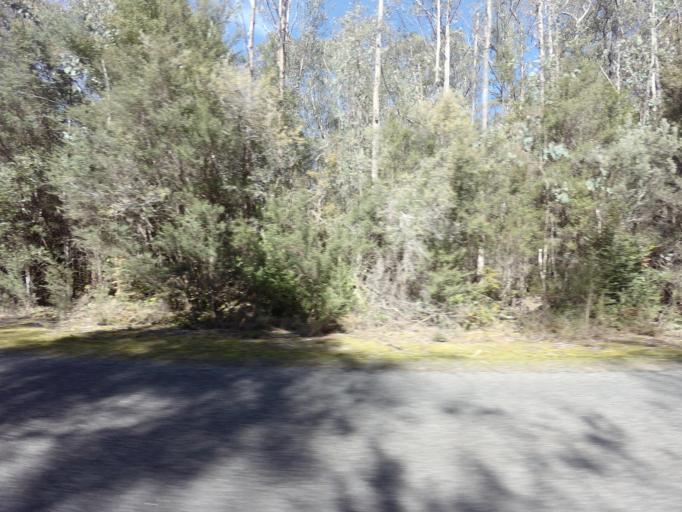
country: AU
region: Tasmania
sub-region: Derwent Valley
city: New Norfolk
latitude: -42.7362
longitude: 146.4236
